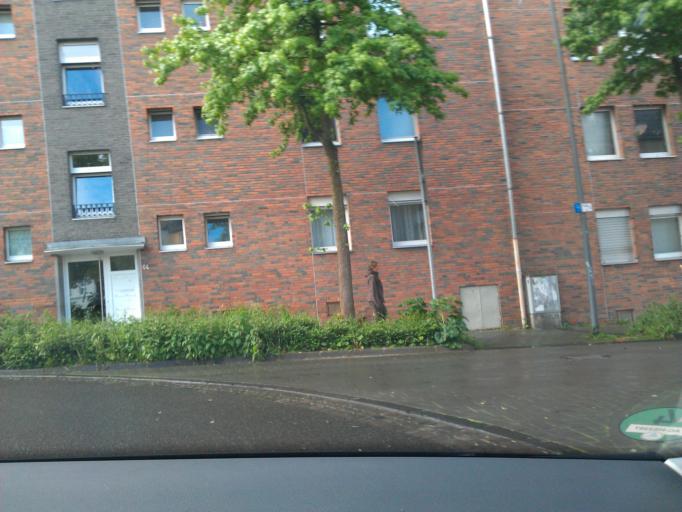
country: DE
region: North Rhine-Westphalia
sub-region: Regierungsbezirk Koln
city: Aachen
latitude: 50.7670
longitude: 6.1082
